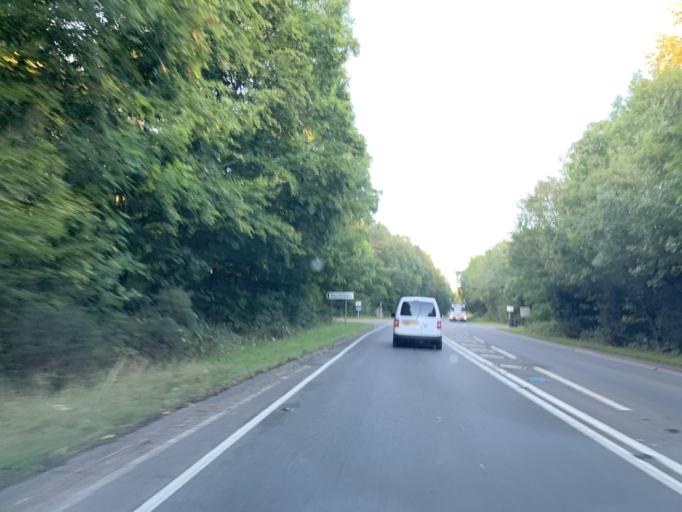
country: GB
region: England
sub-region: Wiltshire
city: Whiteparish
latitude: 50.9860
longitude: -1.6410
